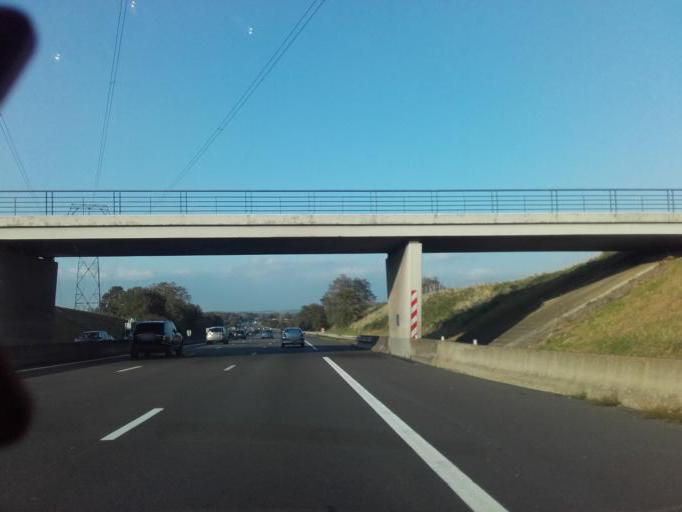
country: FR
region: Bourgogne
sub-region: Departement de Saone-et-Loire
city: Saint-Martin-Belle-Roche
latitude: 46.4281
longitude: 4.8687
